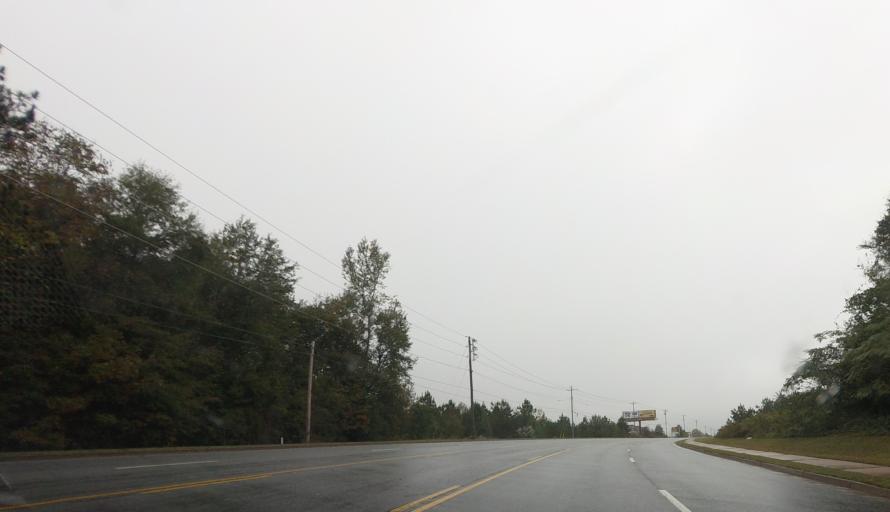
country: US
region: Georgia
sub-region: Houston County
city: Centerville
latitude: 32.6124
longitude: -83.6691
